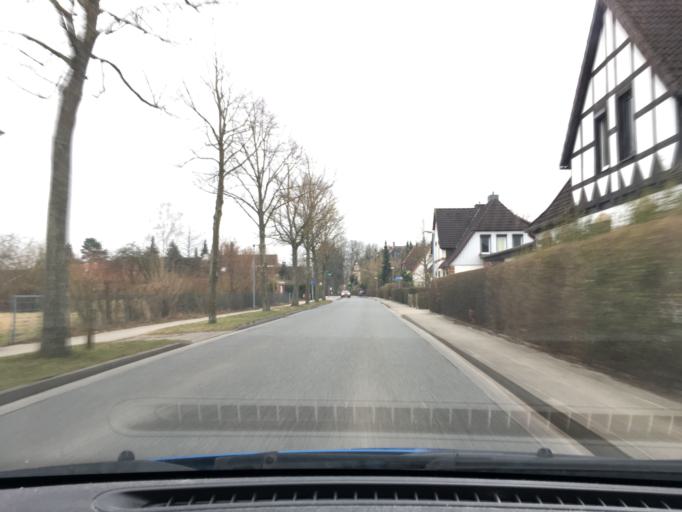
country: DE
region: Lower Saxony
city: Lueneburg
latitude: 53.2583
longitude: 10.3857
